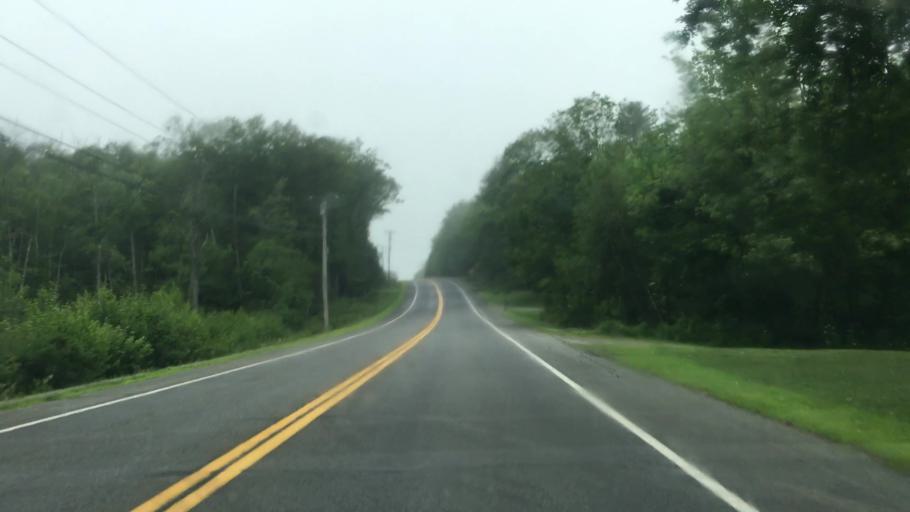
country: US
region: Maine
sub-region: Lincoln County
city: Wiscasset
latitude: 44.0461
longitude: -69.6779
